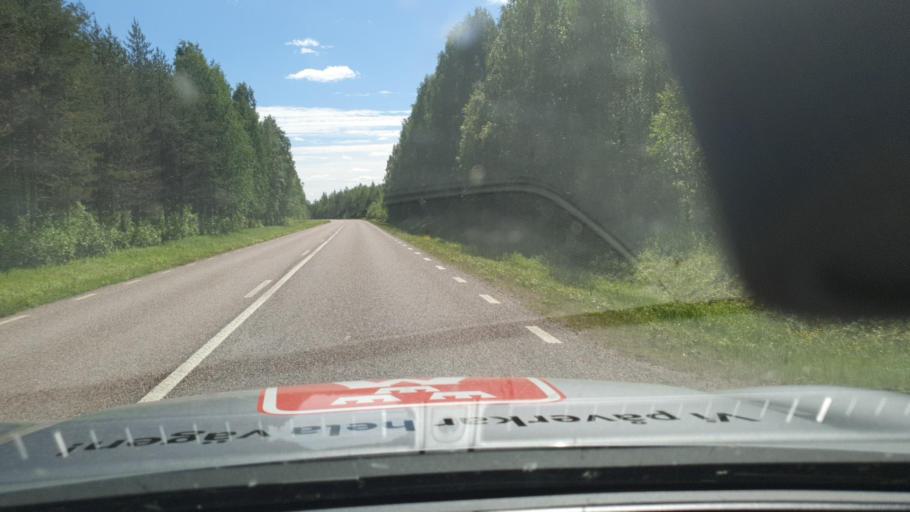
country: FI
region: Lapland
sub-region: Tunturi-Lappi
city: Kolari
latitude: 67.0515
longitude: 23.6790
